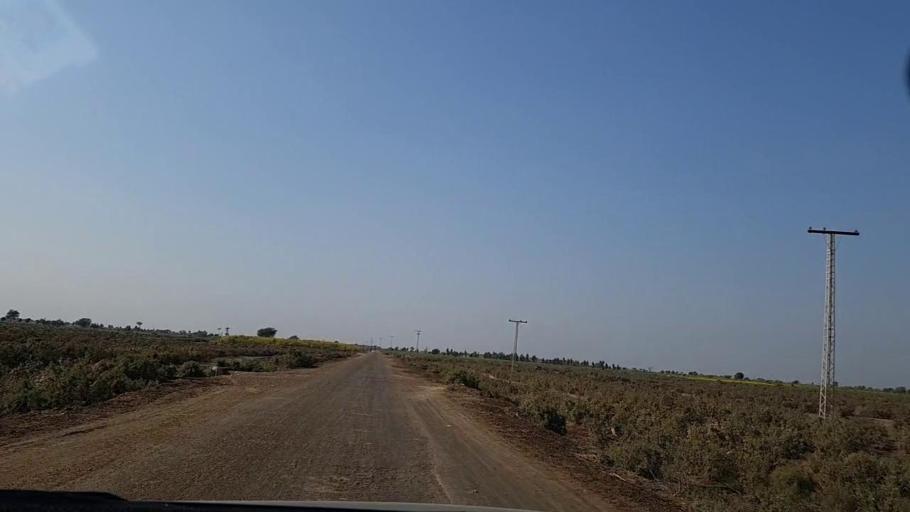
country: PK
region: Sindh
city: Digri
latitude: 25.1687
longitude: 69.0214
